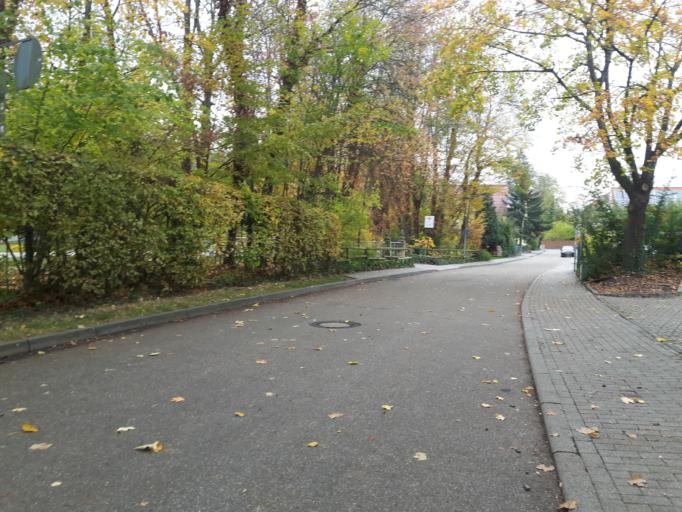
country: DE
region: Baden-Wuerttemberg
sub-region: Karlsruhe Region
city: Balzfeld
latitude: 49.2336
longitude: 8.7768
